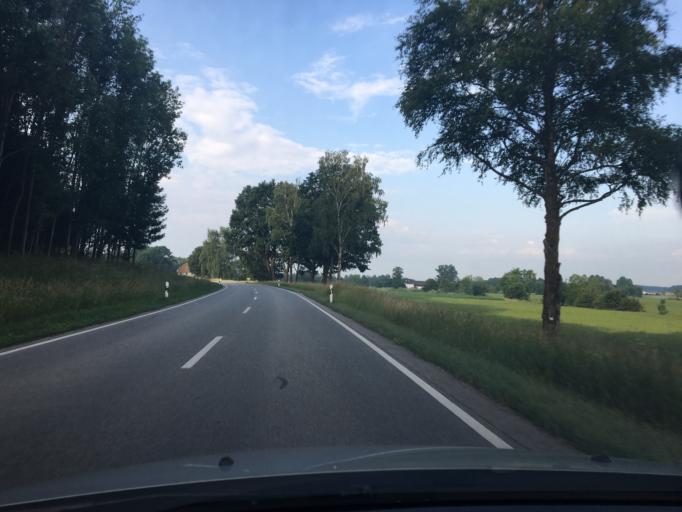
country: DE
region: Bavaria
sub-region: Lower Bavaria
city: Vilsbiburg
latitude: 48.4220
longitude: 12.3416
